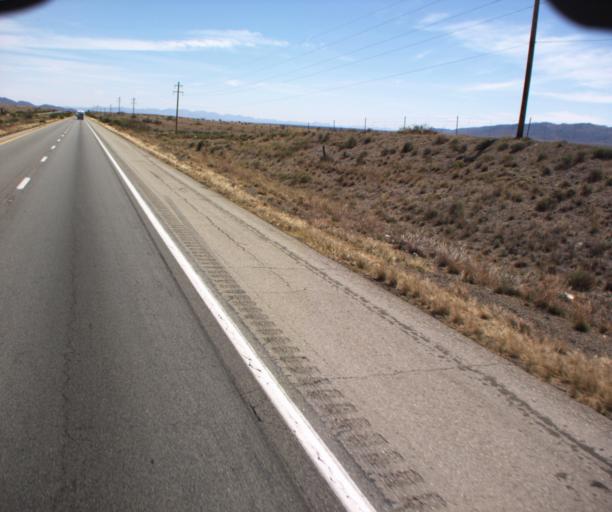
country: US
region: Arizona
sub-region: Cochise County
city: Willcox
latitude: 32.3498
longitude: -109.7356
